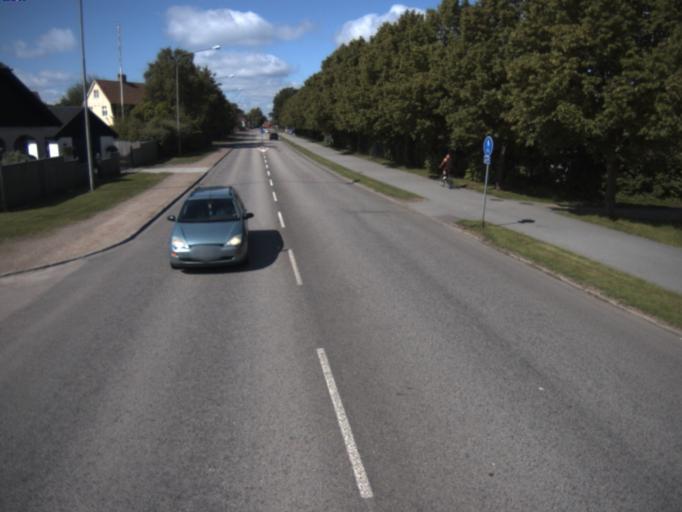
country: SE
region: Skane
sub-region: Helsingborg
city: Helsingborg
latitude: 56.0516
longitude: 12.7179
